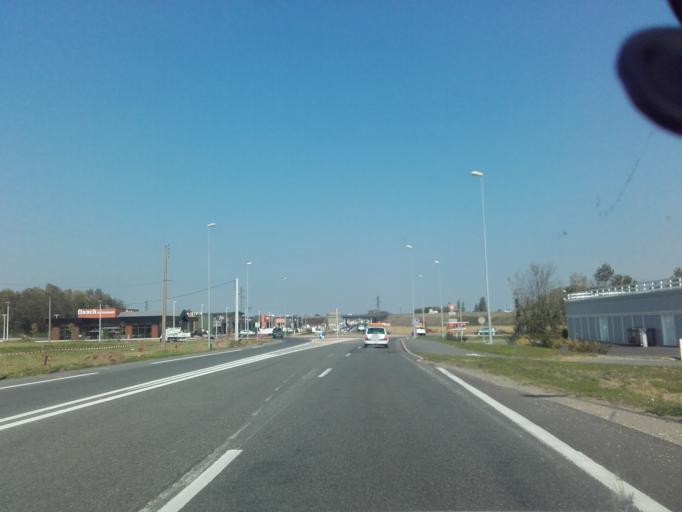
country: FR
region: Bourgogne
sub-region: Departement de Saone-et-Loire
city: Creches-sur-Saone
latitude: 46.2569
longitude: 4.7905
